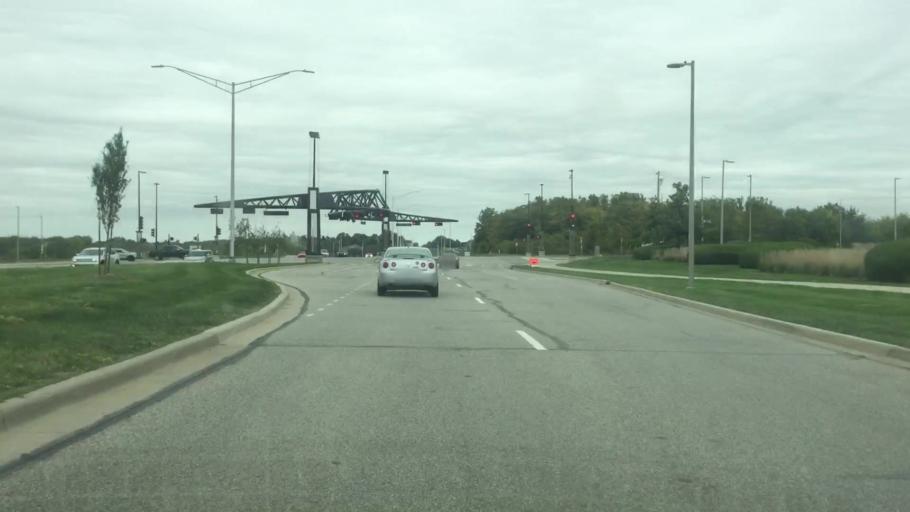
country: US
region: Kansas
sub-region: Johnson County
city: Lenexa
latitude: 38.9699
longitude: -94.7796
